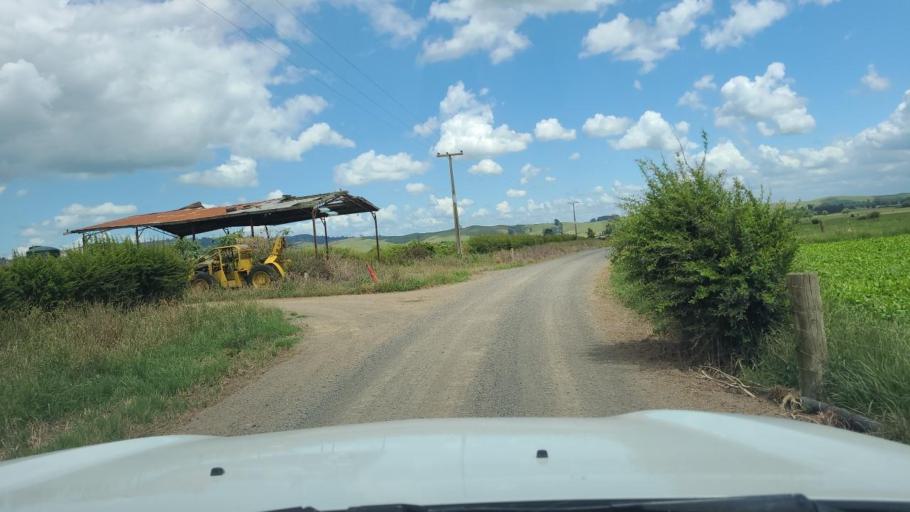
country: NZ
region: Waikato
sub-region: Hauraki District
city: Ngatea
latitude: -37.5197
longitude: 175.4123
